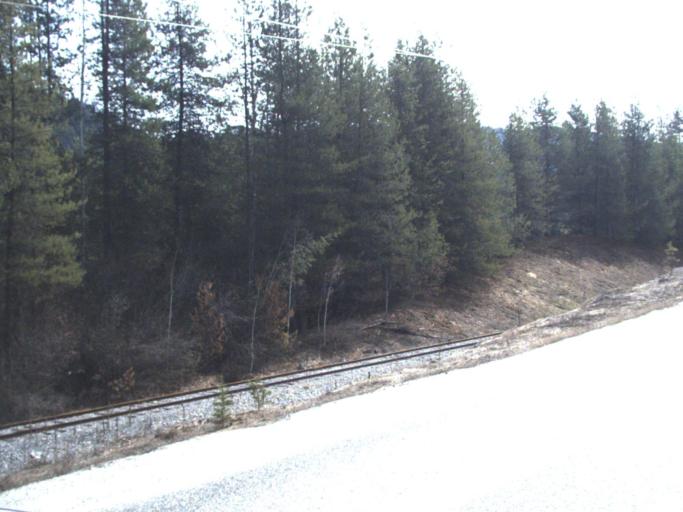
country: US
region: Washington
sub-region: Stevens County
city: Chewelah
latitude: 48.6433
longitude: -117.3751
